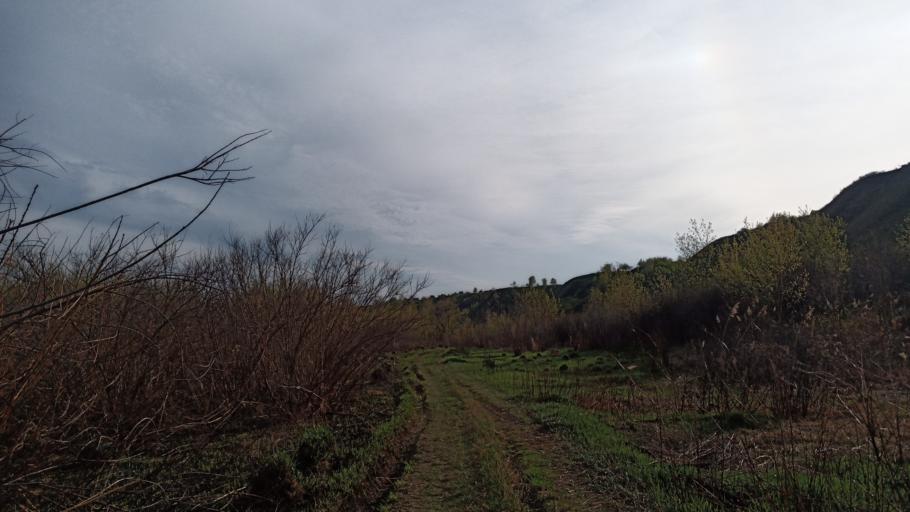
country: RU
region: Altai Krai
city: Yuzhnyy
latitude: 53.2235
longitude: 83.7277
